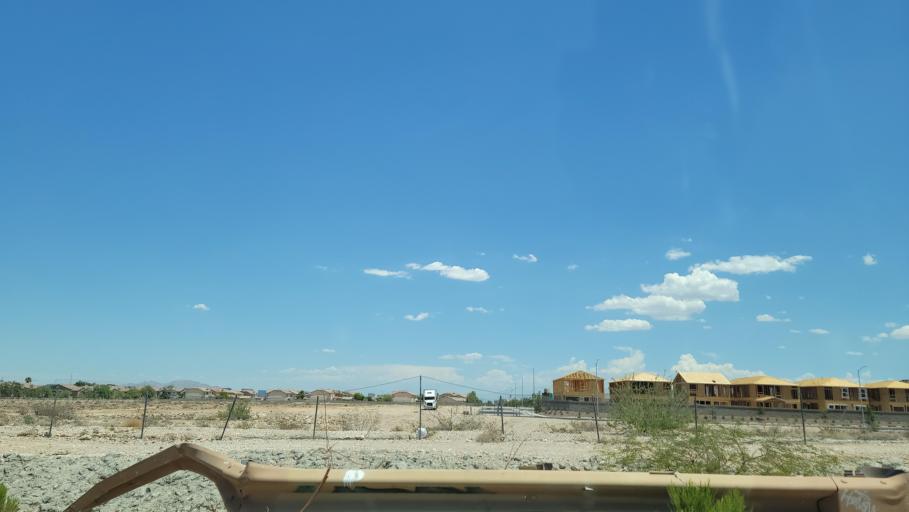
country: US
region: Nevada
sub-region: Clark County
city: Spring Valley
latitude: 36.0814
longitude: -115.2713
